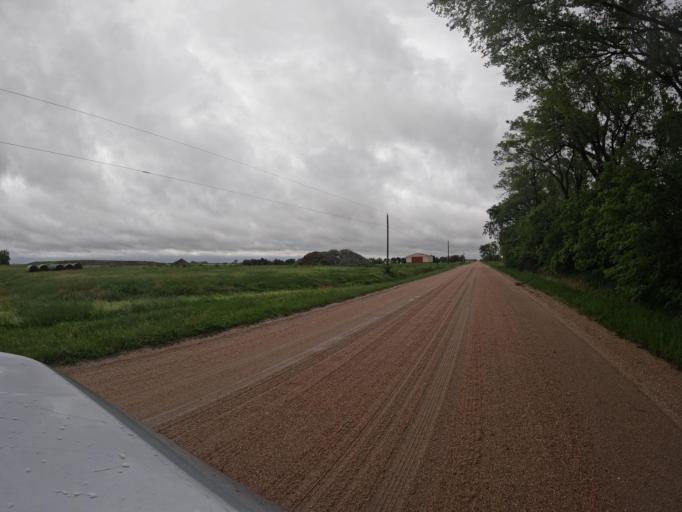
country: US
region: Nebraska
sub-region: Clay County
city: Harvard
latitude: 40.6270
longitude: -98.0992
